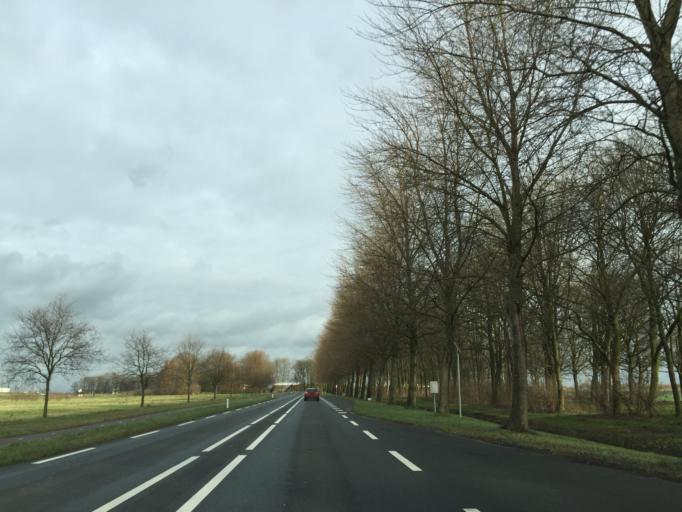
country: NL
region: South Holland
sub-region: Gemeente Rijnwoude
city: Benthuizen
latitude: 52.0589
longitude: 4.5549
